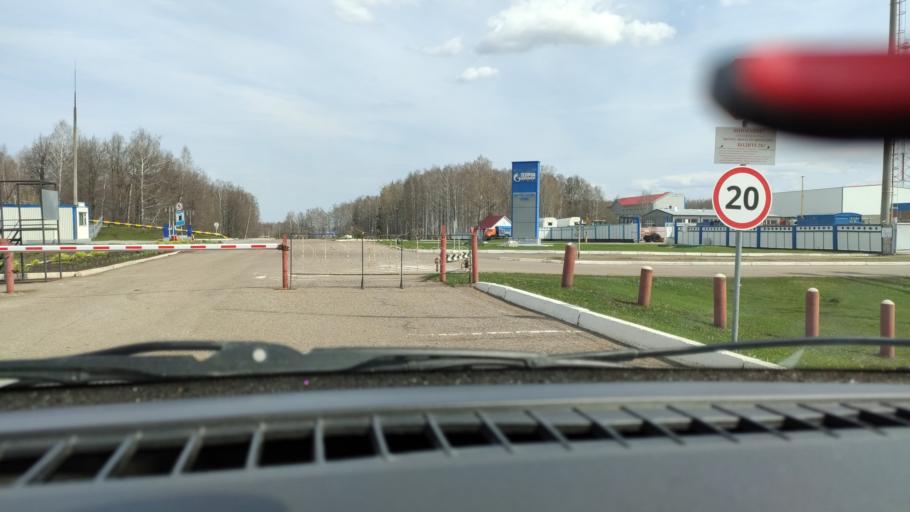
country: RU
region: Bashkortostan
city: Dyurtyuli
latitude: 55.2850
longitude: 55.0707
